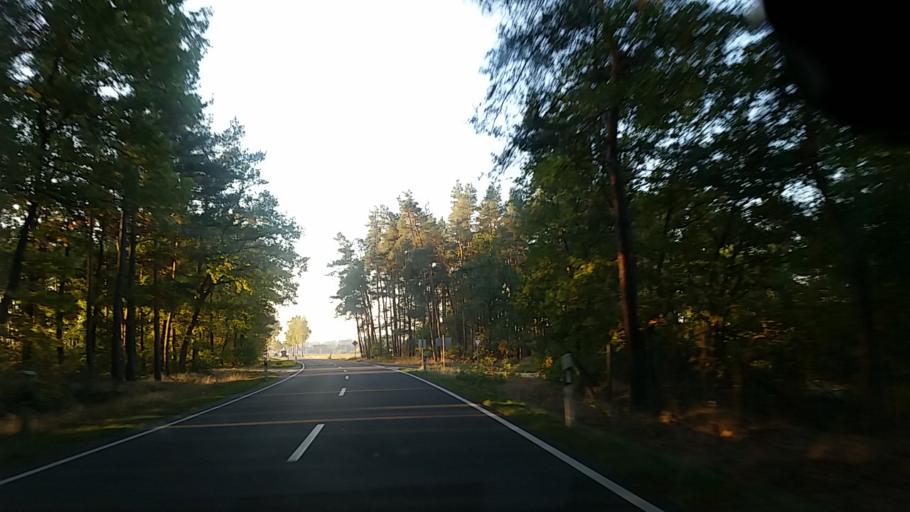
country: DE
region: Lower Saxony
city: Barwedel
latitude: 52.5804
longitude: 10.7873
